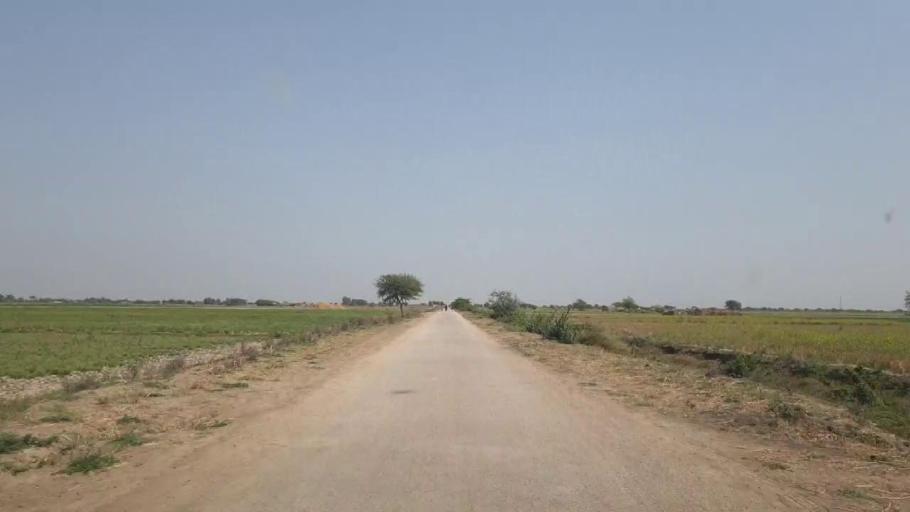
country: PK
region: Sindh
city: Jati
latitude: 24.4774
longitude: 68.5581
